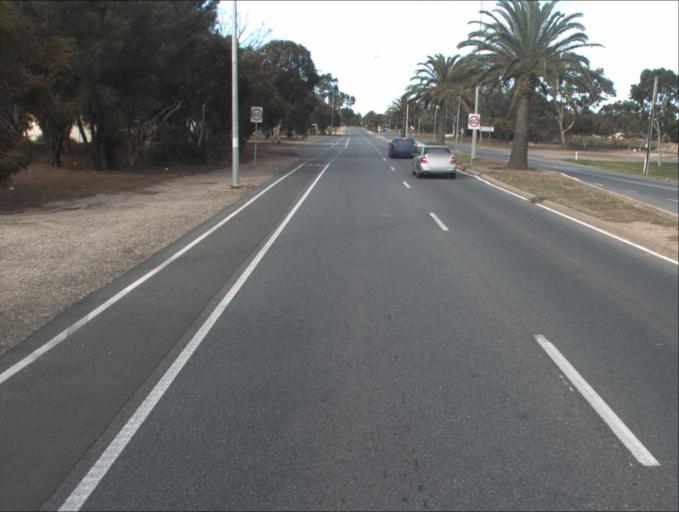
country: AU
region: South Australia
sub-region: Charles Sturt
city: West Lakes Shore
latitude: -34.8533
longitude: 138.5023
